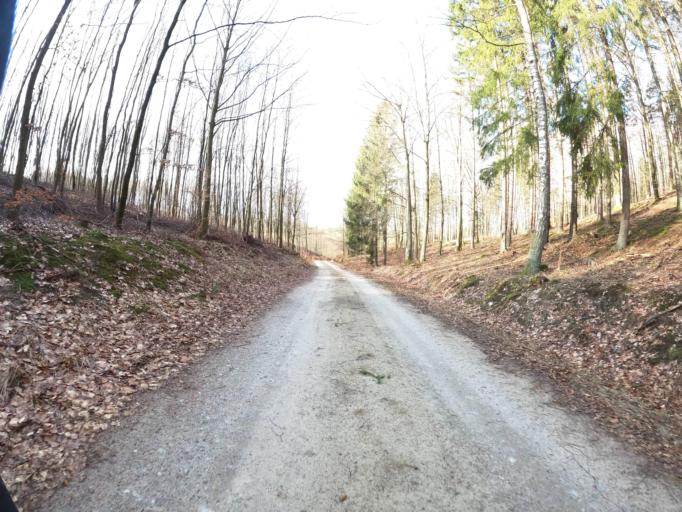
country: PL
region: West Pomeranian Voivodeship
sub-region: Powiat koszalinski
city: Polanow
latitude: 54.2313
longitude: 16.6811
